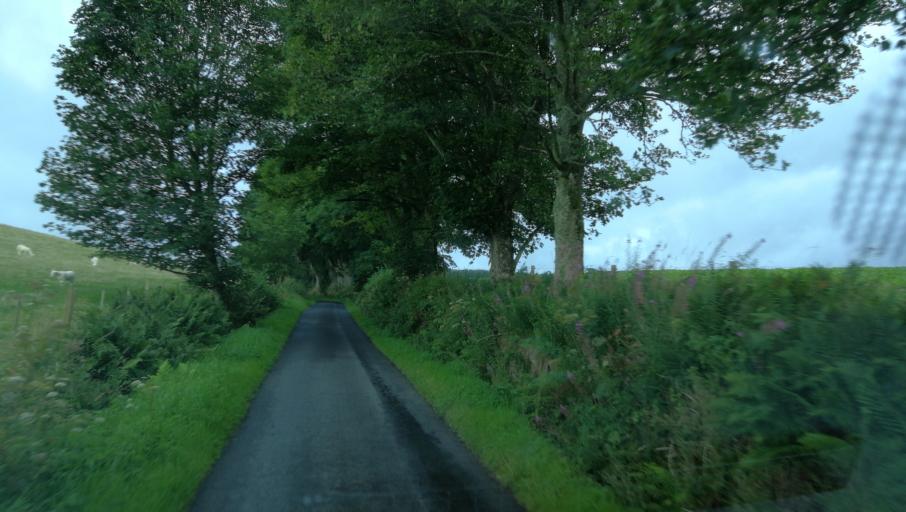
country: GB
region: Scotland
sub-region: Perth and Kinross
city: Alyth
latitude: 56.6262
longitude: -3.2662
